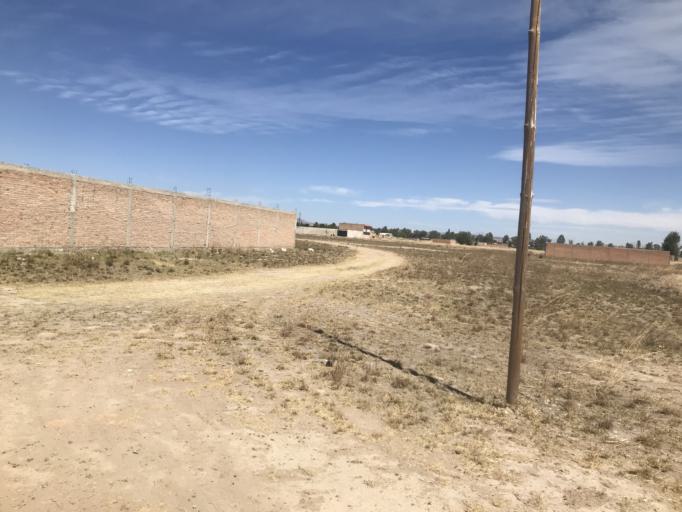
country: MX
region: Durango
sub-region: Durango
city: Sebastian Lerdo de Tejada
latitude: 23.9761
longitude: -104.6549
